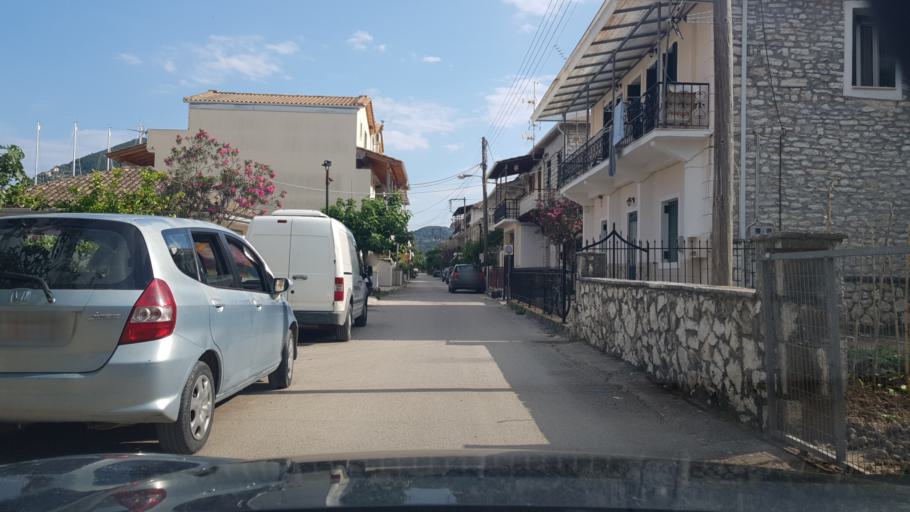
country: GR
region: Ionian Islands
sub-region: Lefkada
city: Nidri
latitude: 38.6866
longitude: 20.6983
